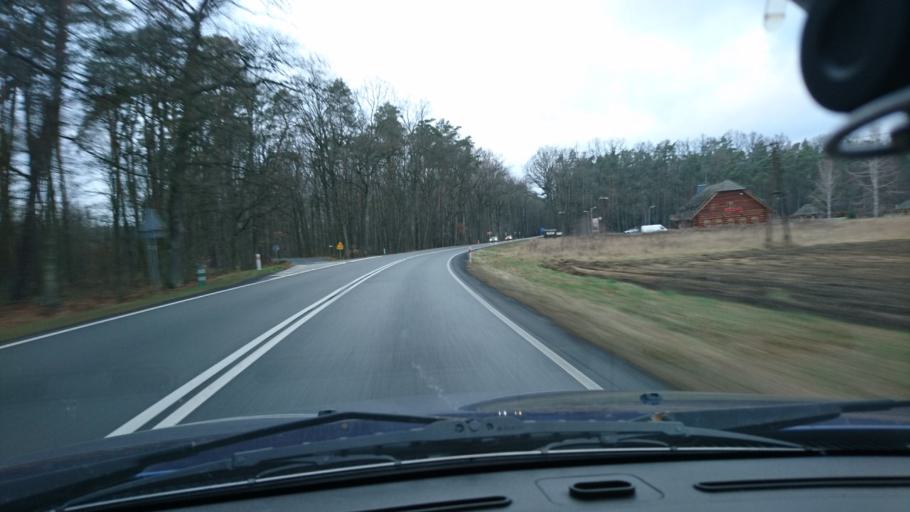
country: PL
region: Opole Voivodeship
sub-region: Powiat oleski
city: Olesno
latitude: 50.9208
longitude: 18.3397
